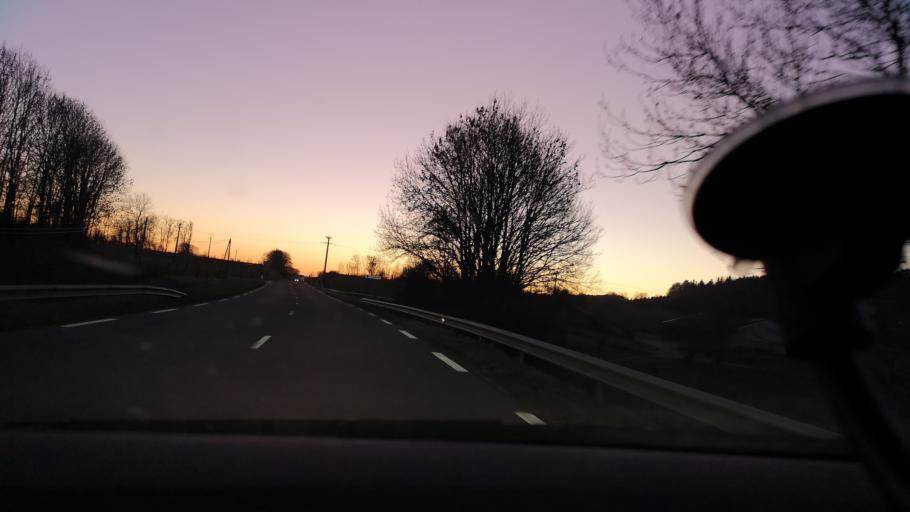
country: FR
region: Franche-Comte
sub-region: Departement du Jura
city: Champagnole
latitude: 46.8100
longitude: 6.0303
